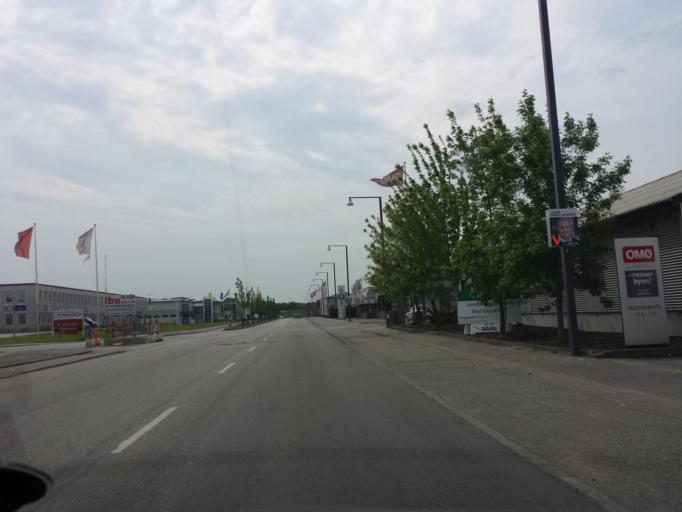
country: DK
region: Capital Region
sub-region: Rodovre Kommune
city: Rodovre
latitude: 55.6958
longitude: 12.4326
